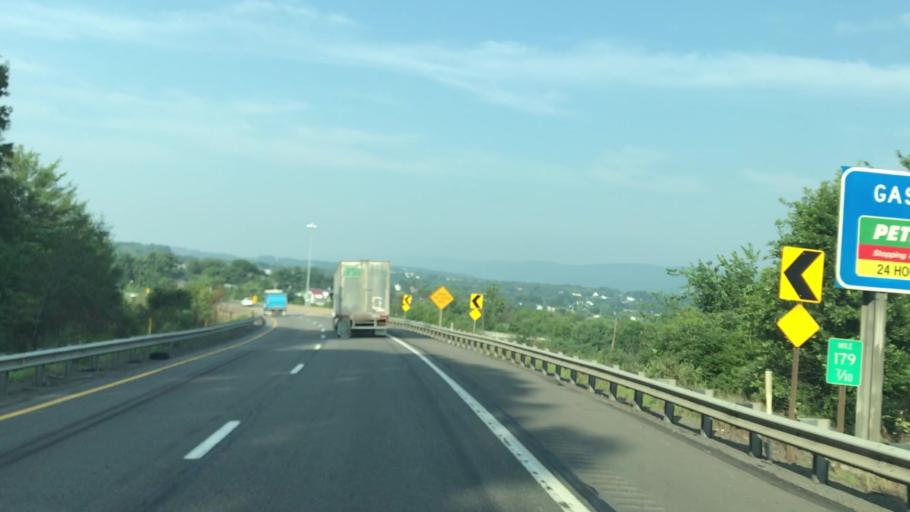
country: US
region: Pennsylvania
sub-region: Lackawanna County
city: Moosic
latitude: 41.3568
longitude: -75.7196
